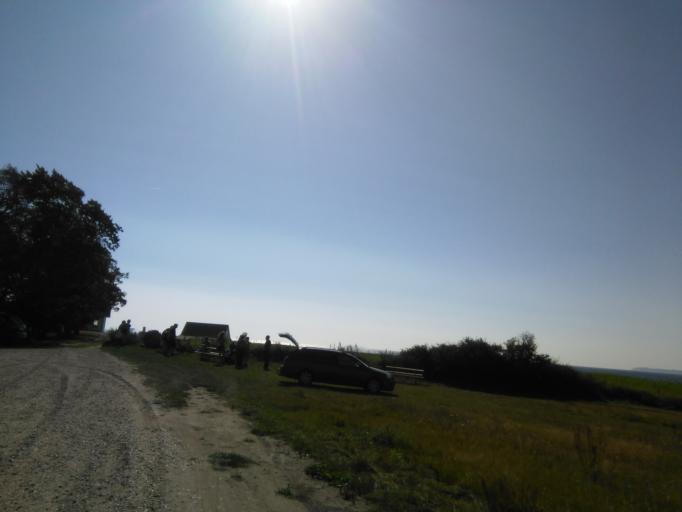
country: DK
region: Central Jutland
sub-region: Syddjurs Kommune
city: Ebeltoft
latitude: 56.2448
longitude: 10.7799
